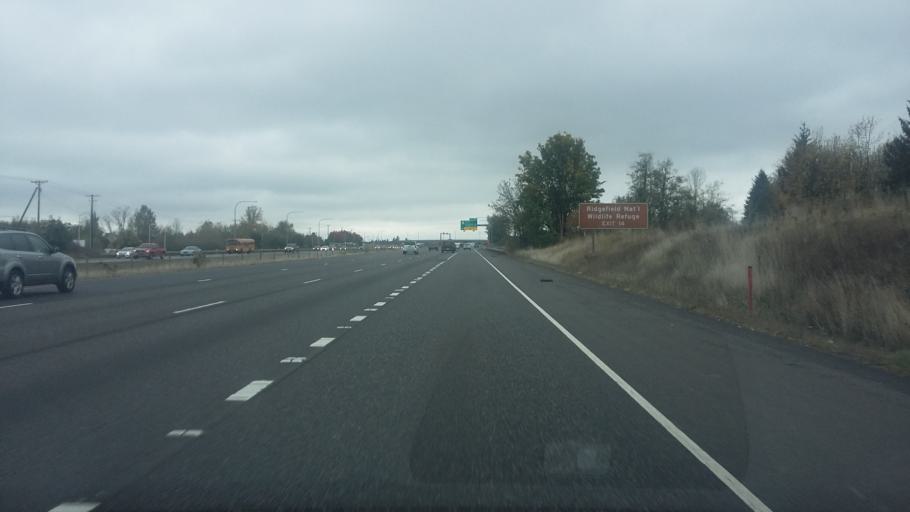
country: US
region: Washington
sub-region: Clark County
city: La Center
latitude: 45.8085
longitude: -122.6822
